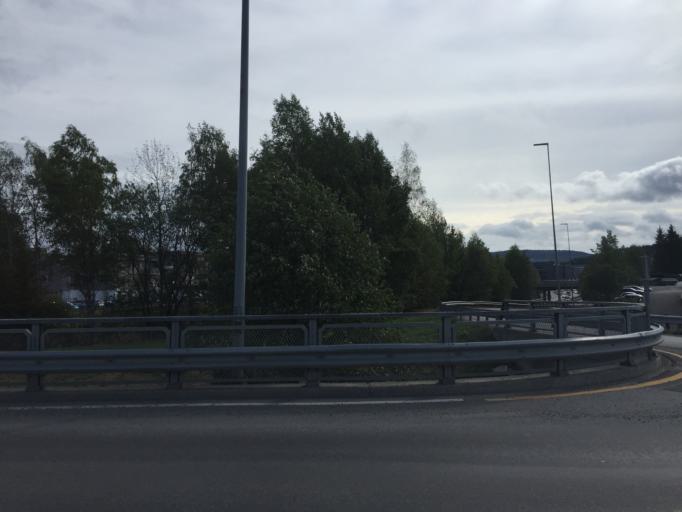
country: NO
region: Akershus
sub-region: Lorenskog
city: Kjenn
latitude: 59.9301
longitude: 10.9466
